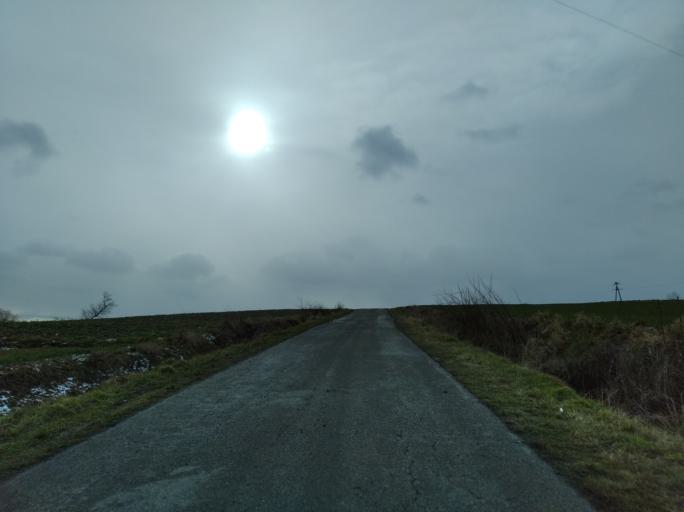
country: PL
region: Subcarpathian Voivodeship
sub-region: Powiat strzyzowski
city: Strzyzow
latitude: 49.8965
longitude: 21.7369
